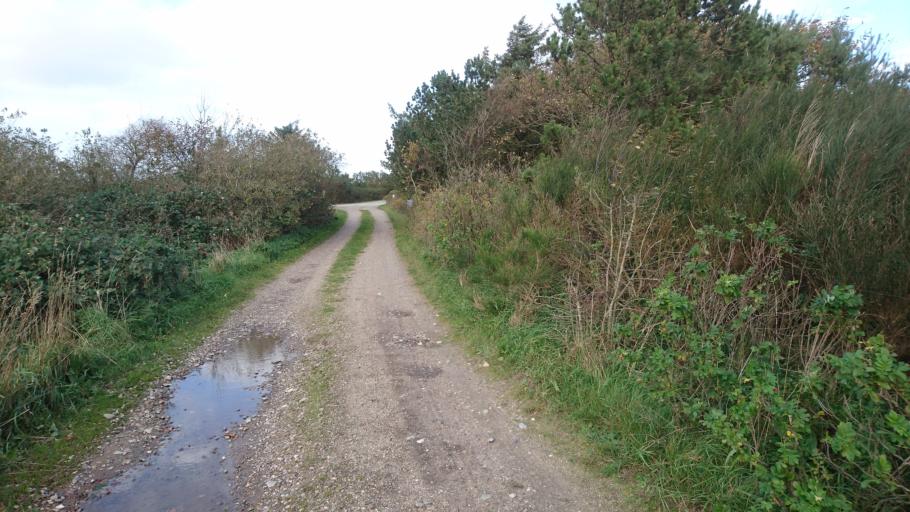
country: DK
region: North Denmark
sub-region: Vesthimmerland Kommune
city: Farso
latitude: 56.8096
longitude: 9.1761
